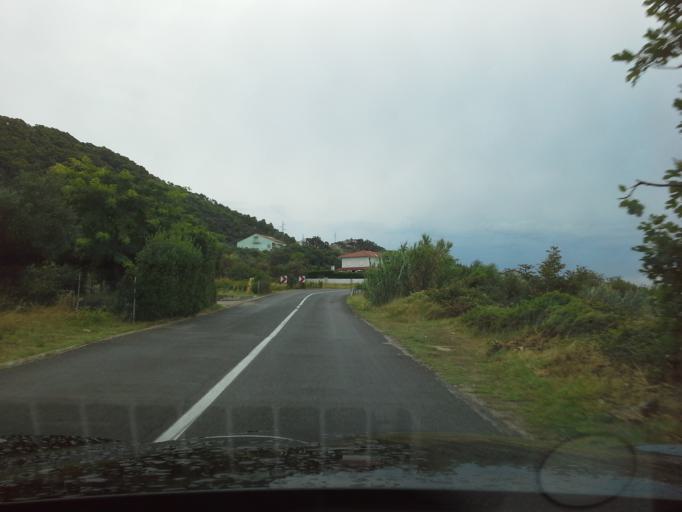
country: HR
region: Primorsko-Goranska
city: Banjol
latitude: 44.7422
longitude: 14.7975
